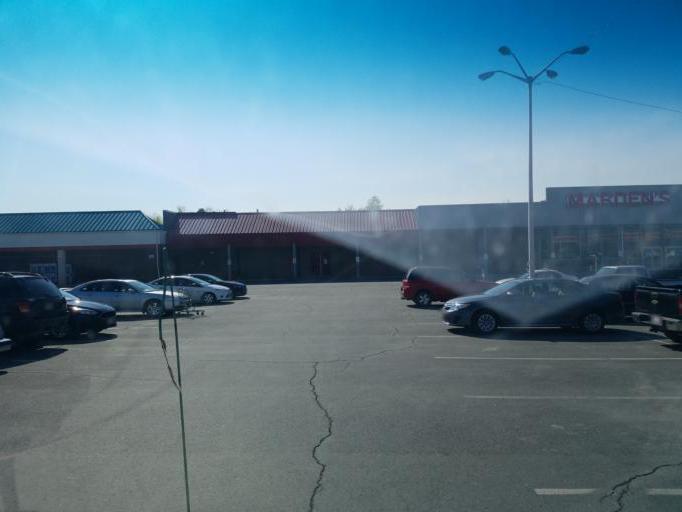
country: US
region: Maine
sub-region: Aroostook County
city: Presque Isle
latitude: 46.6999
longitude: -68.0119
